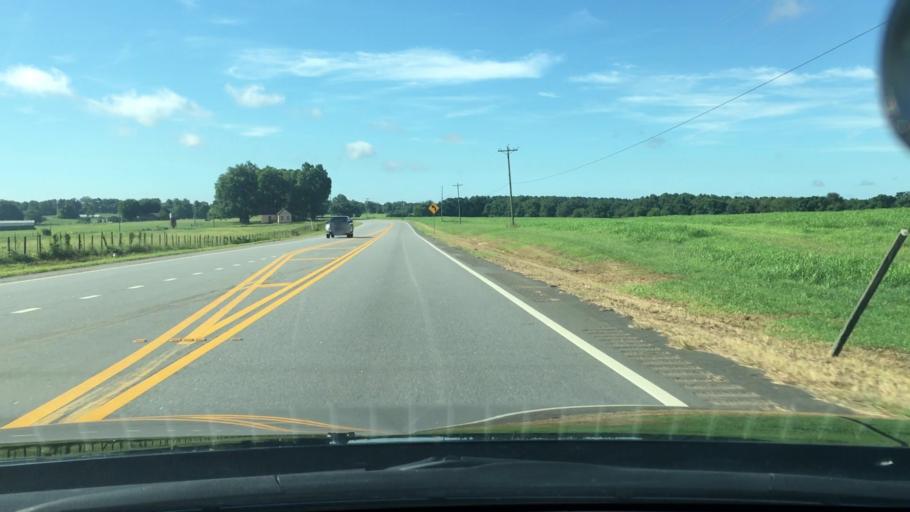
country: US
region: Georgia
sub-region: Morgan County
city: Madison
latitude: 33.4881
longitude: -83.4373
